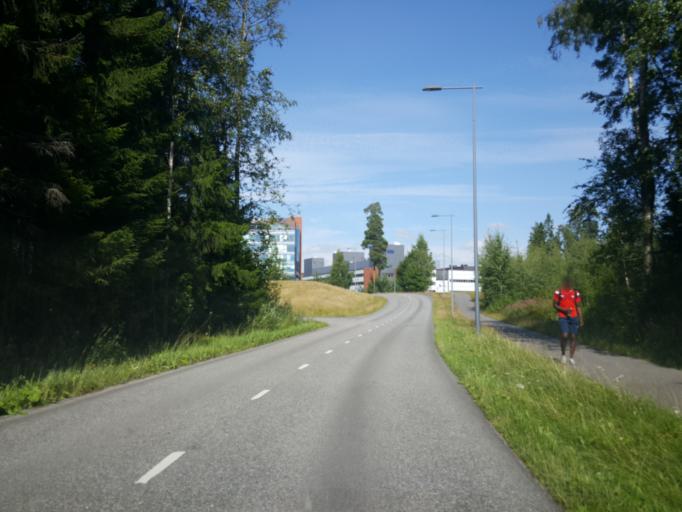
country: FI
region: Uusimaa
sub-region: Helsinki
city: Kilo
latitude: 60.2196
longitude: 24.7550
